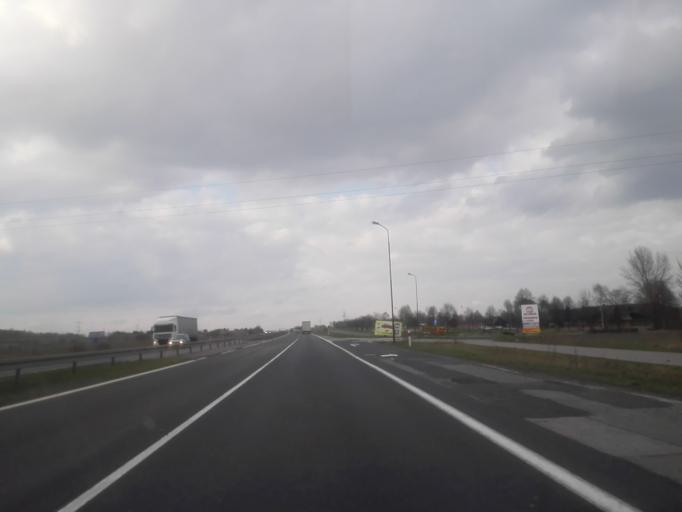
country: PL
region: Lodz Voivodeship
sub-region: Powiat radomszczanski
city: Gomunice
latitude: 51.1768
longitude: 19.4670
